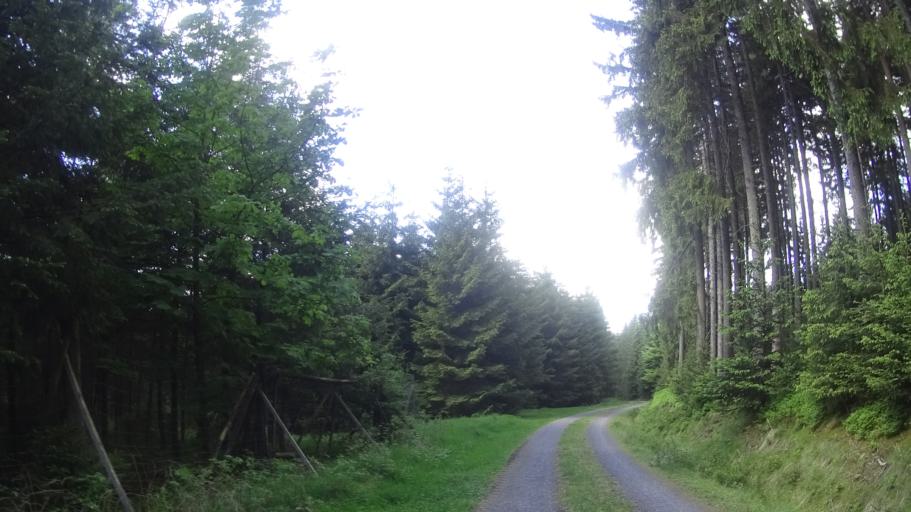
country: DE
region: Thuringia
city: Neustadt am Rennsteig
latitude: 50.5983
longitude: 10.9421
